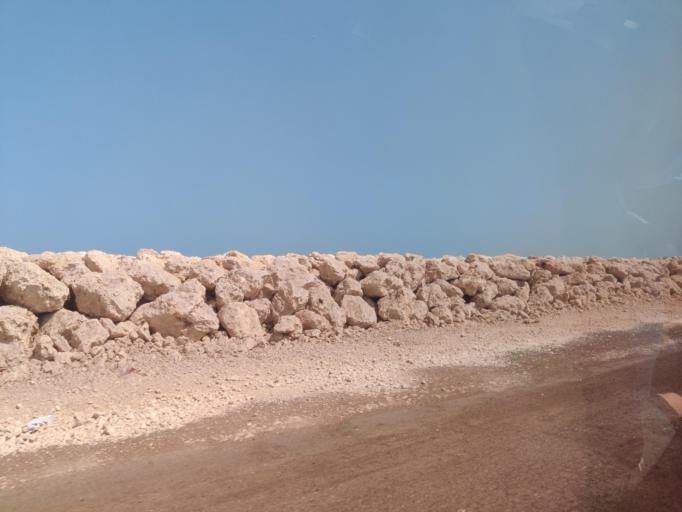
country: CO
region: Bolivar
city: Turbana
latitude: 10.1894
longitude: -75.6374
